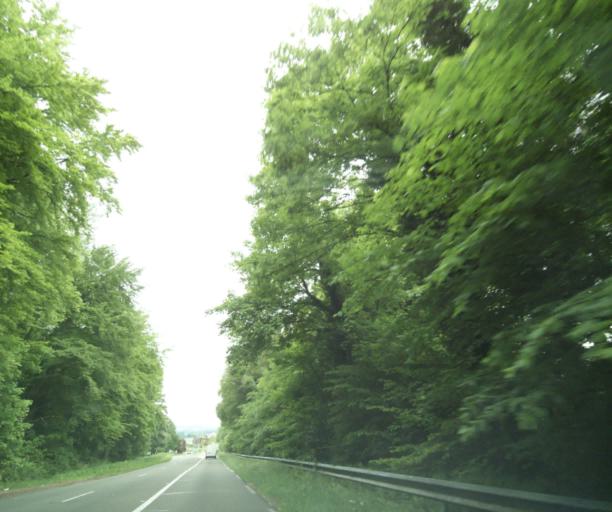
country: FR
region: Ile-de-France
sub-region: Departement des Yvelines
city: Aubergenville
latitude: 48.9614
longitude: 1.8627
